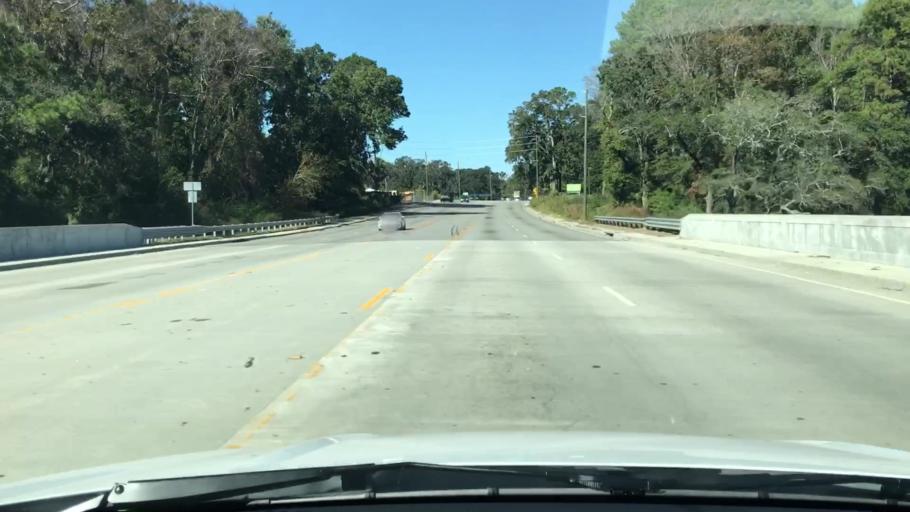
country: US
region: South Carolina
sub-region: Beaufort County
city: Burton
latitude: 32.4502
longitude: -80.7314
